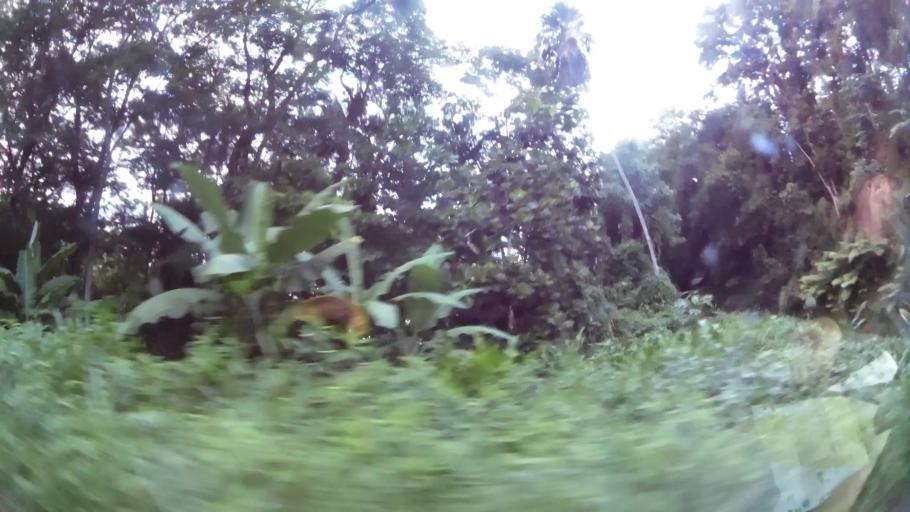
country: DM
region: Saint Andrew
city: Calibishie
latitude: 15.5925
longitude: -61.3773
